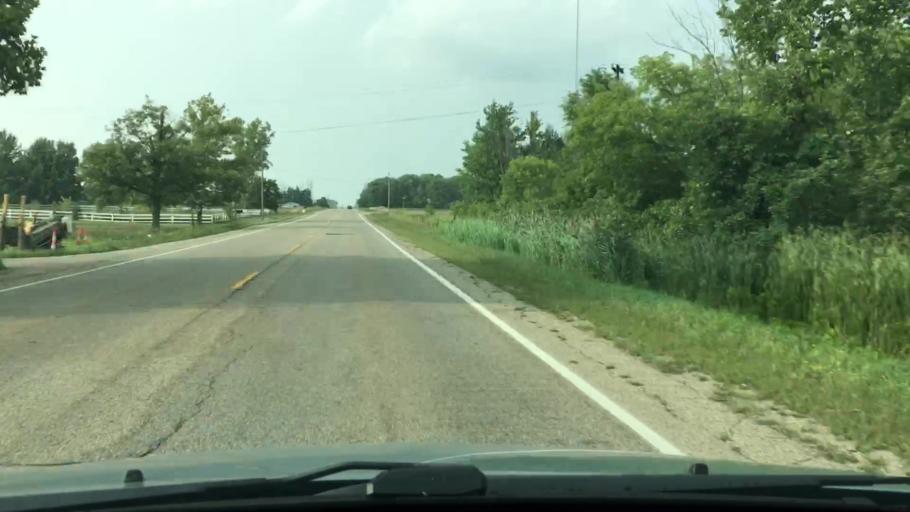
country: US
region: Michigan
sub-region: Ottawa County
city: Allendale
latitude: 42.9488
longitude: -85.9036
